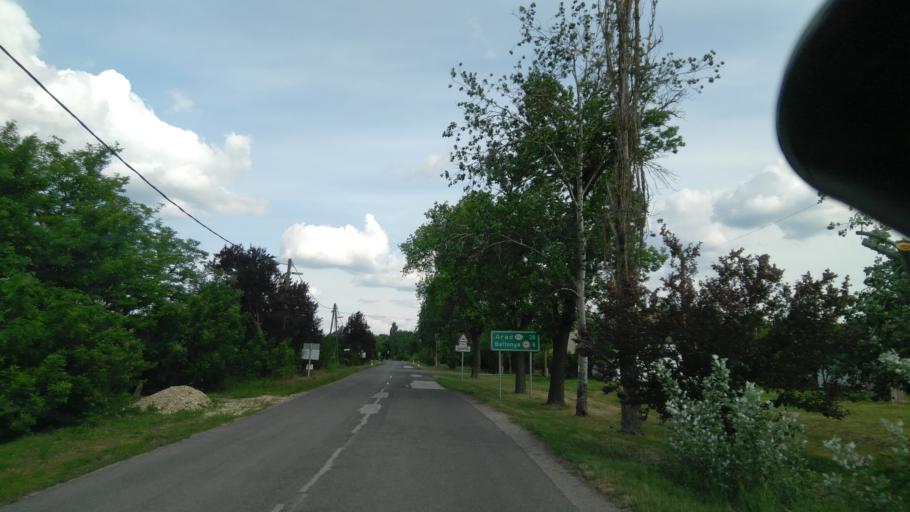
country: HU
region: Bekes
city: Battonya
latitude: 46.2818
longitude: 21.0419
